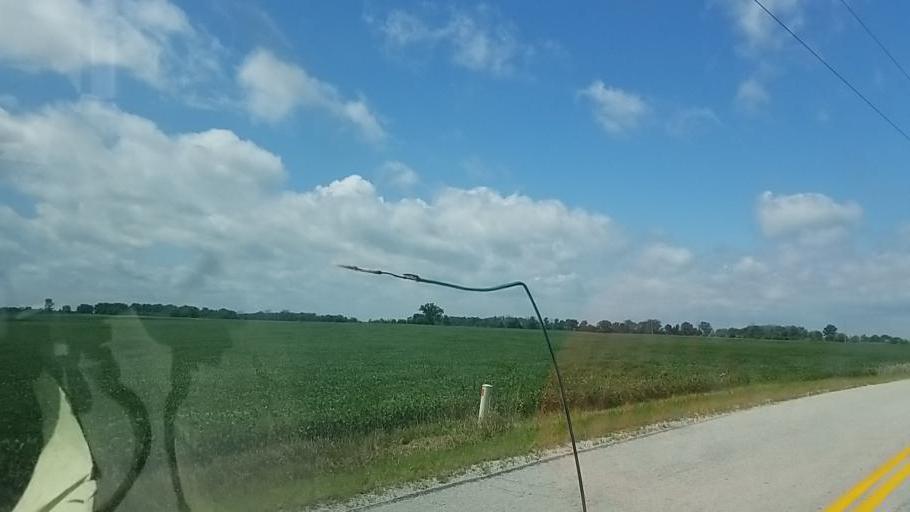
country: US
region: Ohio
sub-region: Clark County
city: South Charleston
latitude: 39.7428
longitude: -83.6597
